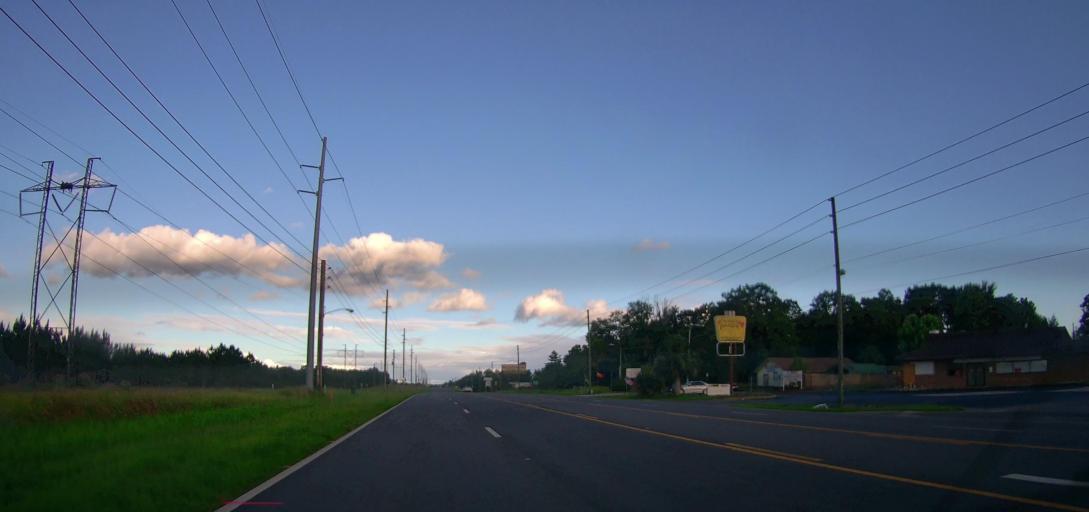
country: US
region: Florida
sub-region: Marion County
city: Silver Springs Shores
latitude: 29.0953
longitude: -82.0030
